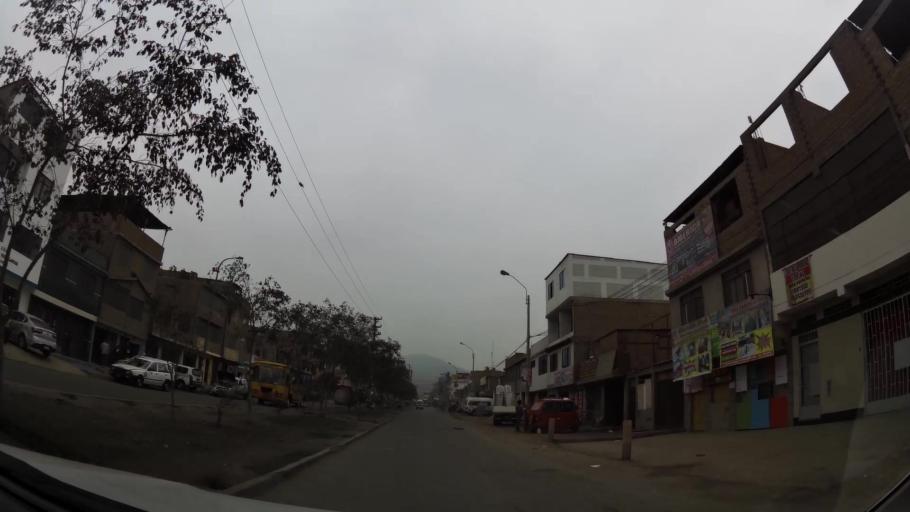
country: PE
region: Lima
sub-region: Lima
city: Independencia
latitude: -11.9465
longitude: -76.9866
